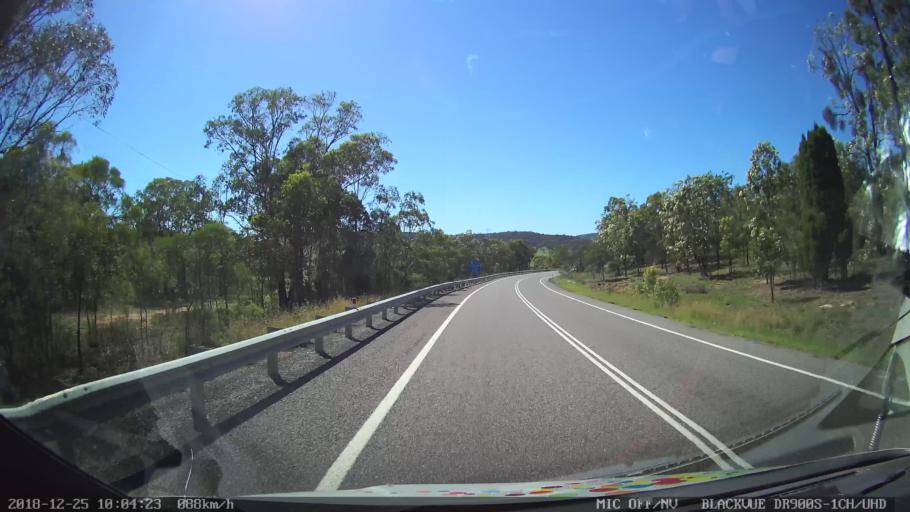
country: AU
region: New South Wales
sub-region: Upper Hunter Shire
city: Merriwa
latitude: -32.2341
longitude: 150.4843
